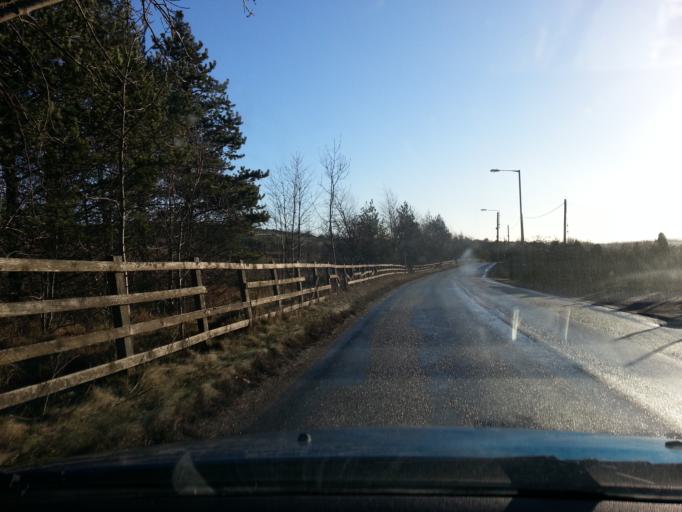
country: GB
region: England
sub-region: County Durham
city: Crook
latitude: 54.7278
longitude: -1.7517
